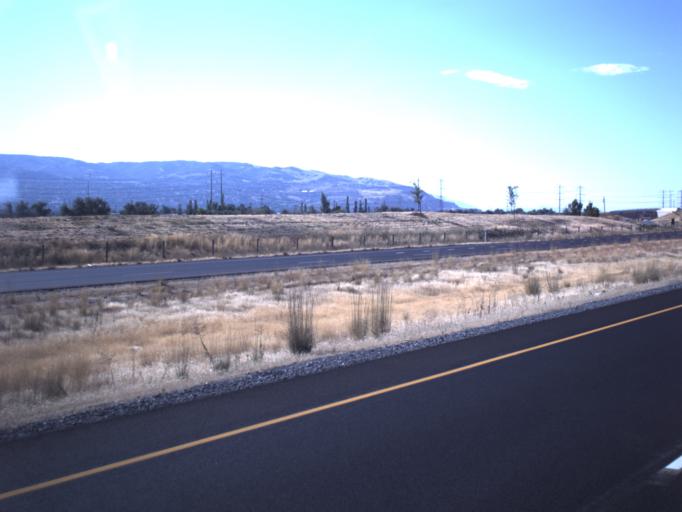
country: US
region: Utah
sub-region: Davis County
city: West Bountiful
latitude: 40.8895
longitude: -111.9362
